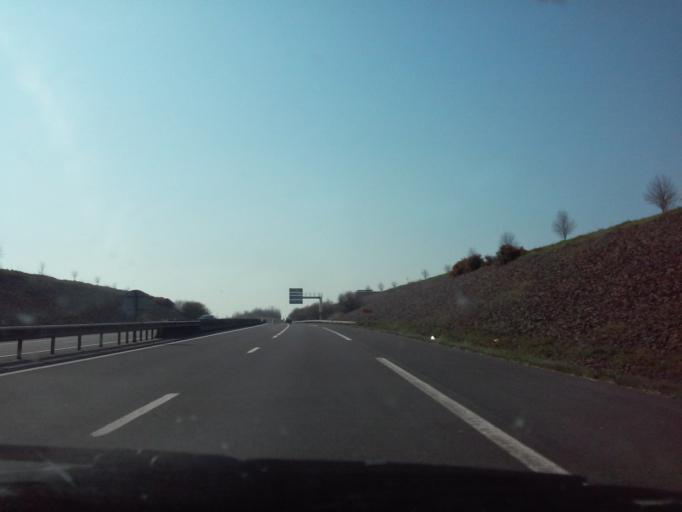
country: FR
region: Lower Normandy
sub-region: Departement du Calvados
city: Saint-Vigor-le-Grand
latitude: 49.2520
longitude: -0.6405
